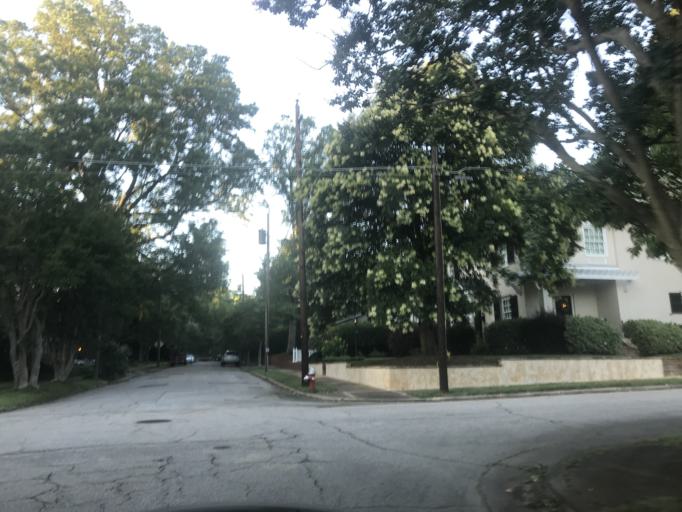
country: US
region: North Carolina
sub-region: Wake County
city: West Raleigh
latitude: 35.7996
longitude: -78.6421
